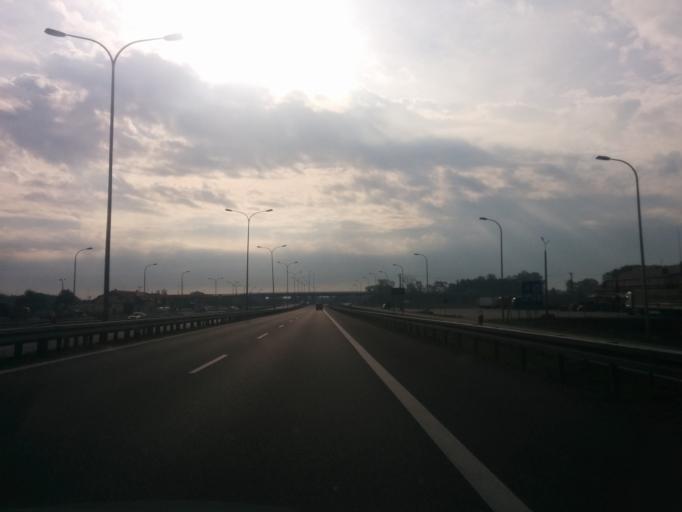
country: PL
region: Masovian Voivodeship
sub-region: Powiat bialobrzeski
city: Stara Blotnica
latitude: 51.5715
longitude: 21.0178
